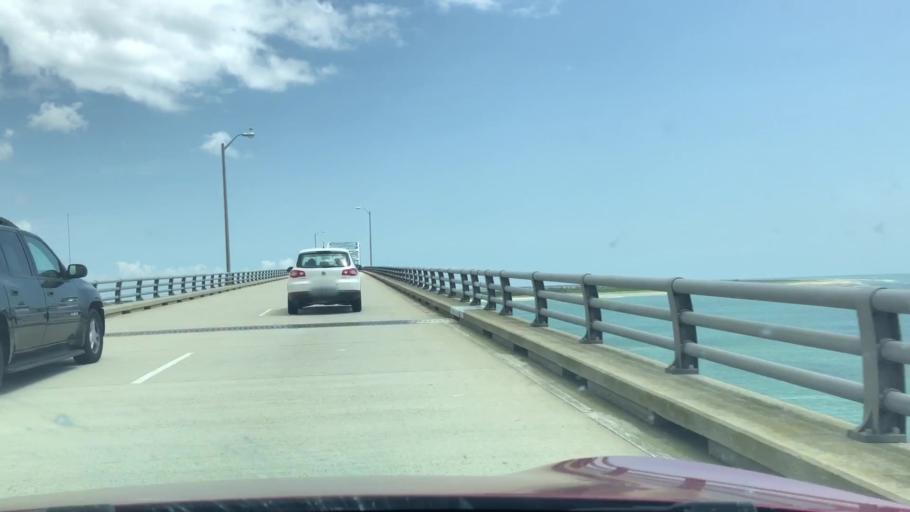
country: US
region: Virginia
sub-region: Northampton County
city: Cape Charles
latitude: 37.0879
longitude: -75.9906
